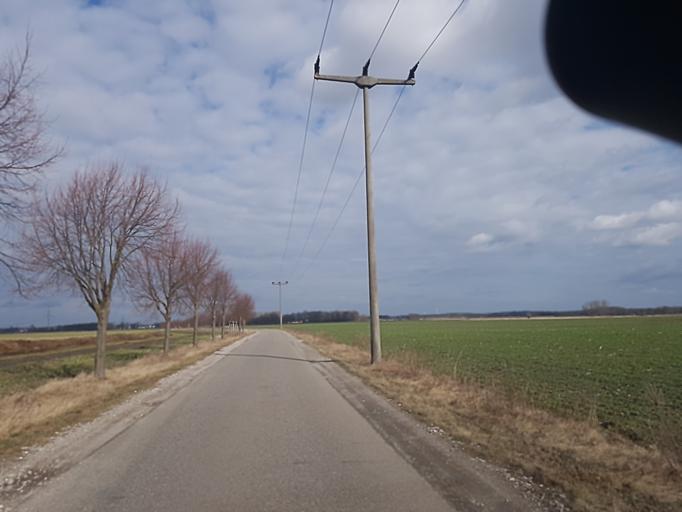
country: DE
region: Brandenburg
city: Schonborn
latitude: 51.5719
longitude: 13.5228
